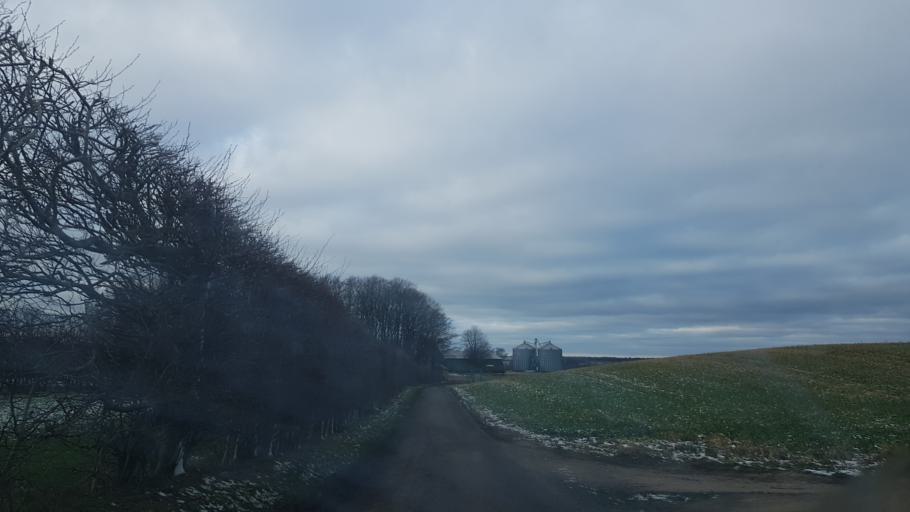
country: DK
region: Zealand
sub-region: Odsherred Kommune
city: Hojby
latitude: 55.9246
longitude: 11.5909
